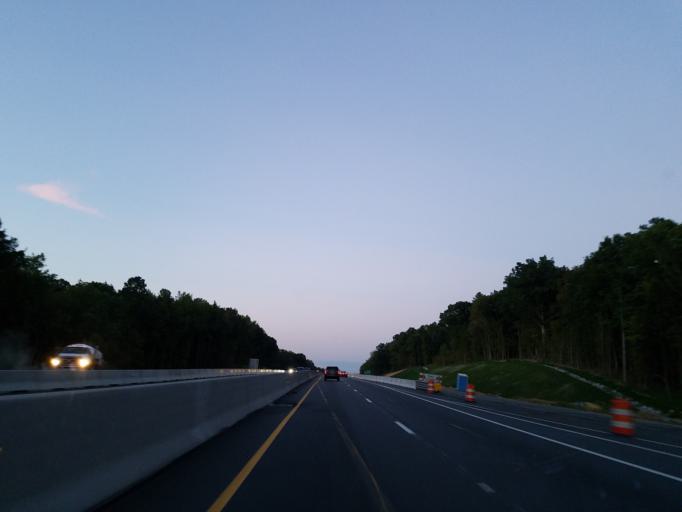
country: US
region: North Carolina
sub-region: Cabarrus County
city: Kannapolis
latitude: 35.4840
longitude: -80.5748
